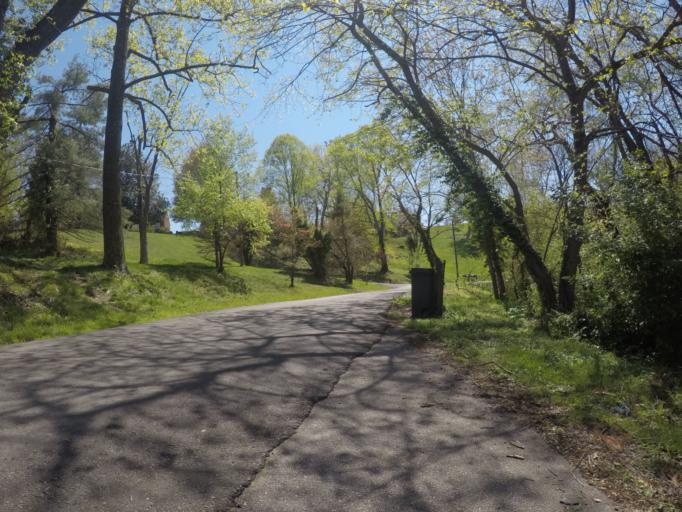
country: US
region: West Virginia
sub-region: Wayne County
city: Kenova
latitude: 38.3943
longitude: -82.5812
